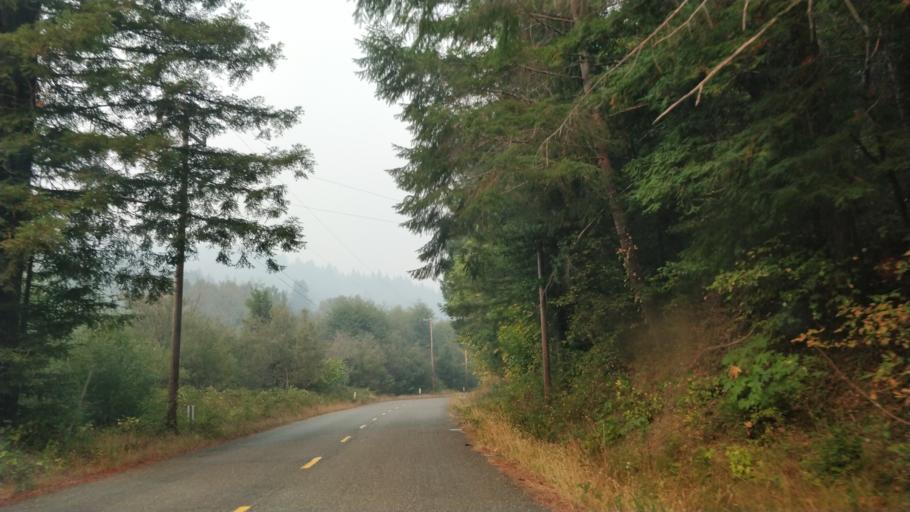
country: US
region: California
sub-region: Humboldt County
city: Rio Dell
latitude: 40.3481
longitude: -124.0231
